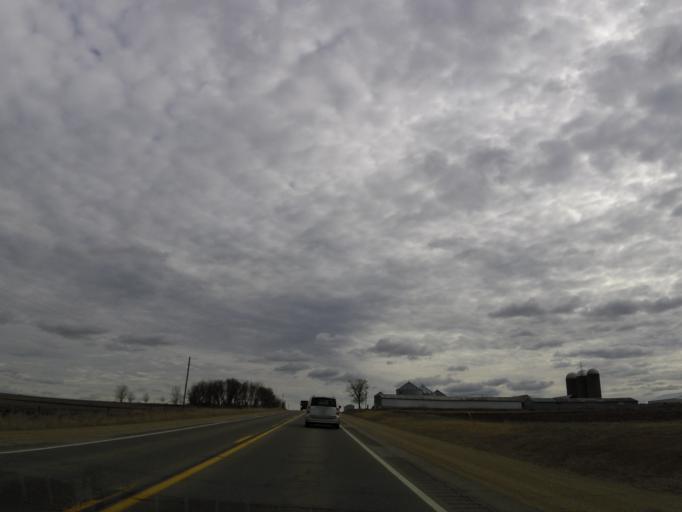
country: US
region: Iowa
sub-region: Chickasaw County
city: New Hampton
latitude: 43.1796
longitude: -92.2986
